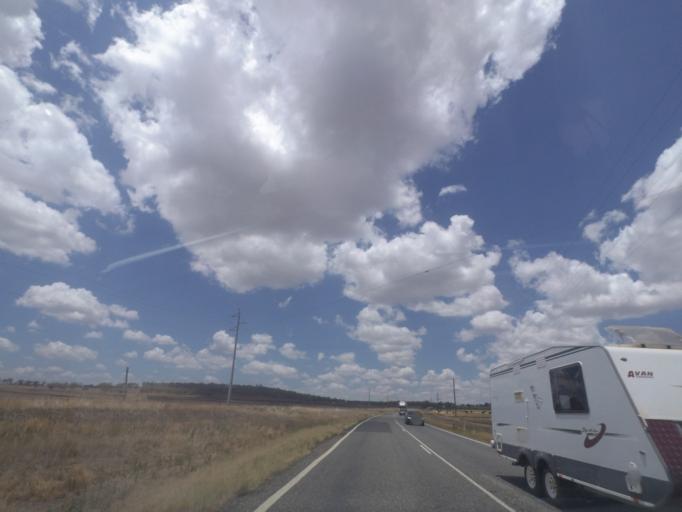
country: AU
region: Queensland
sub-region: Toowoomba
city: Top Camp
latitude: -27.8704
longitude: 151.9606
